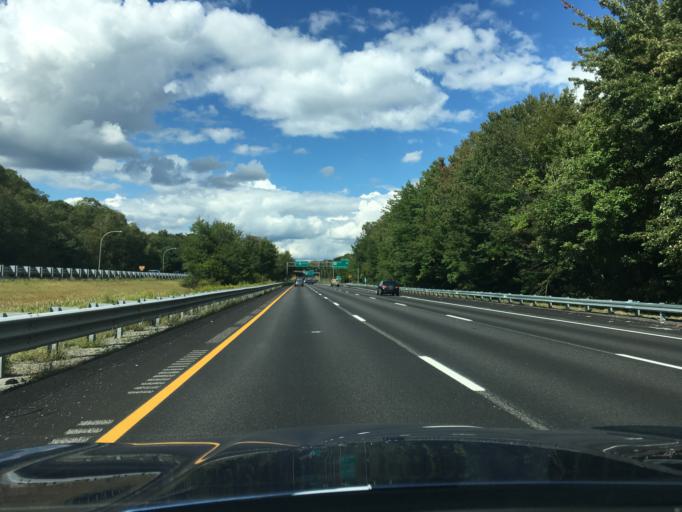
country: US
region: Rhode Island
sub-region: Kent County
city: East Greenwich
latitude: 41.6585
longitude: -71.4896
